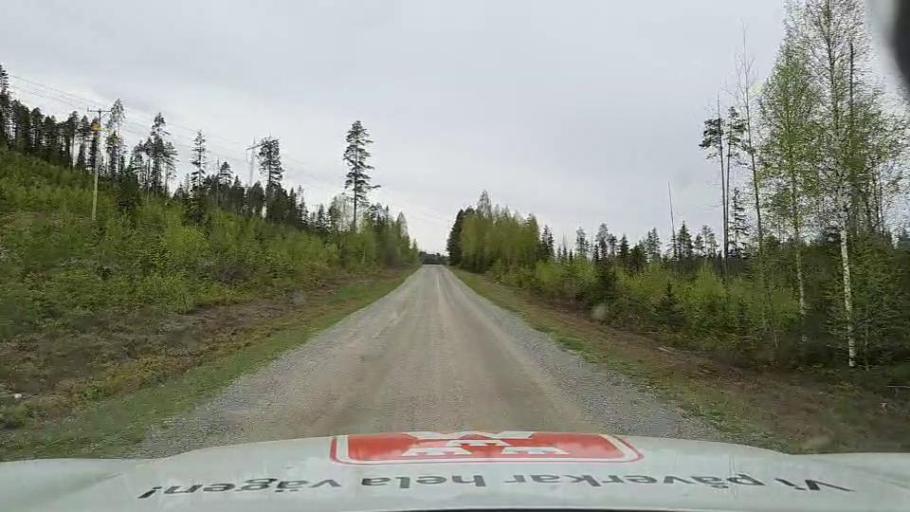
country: SE
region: Jaemtland
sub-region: Bergs Kommun
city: Hoverberg
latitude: 62.5290
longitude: 14.7104
